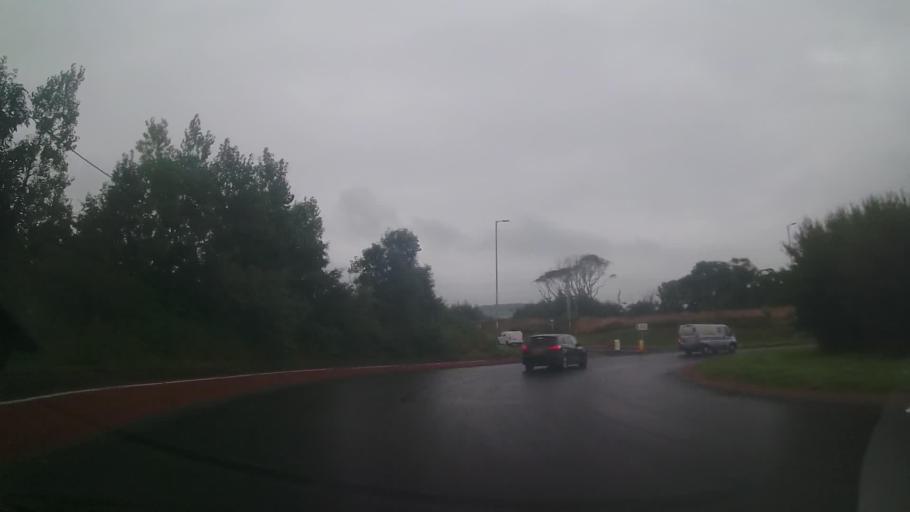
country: GB
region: Scotland
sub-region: North Ayrshire
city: Ardrossan
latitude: 55.6613
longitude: -4.8087
